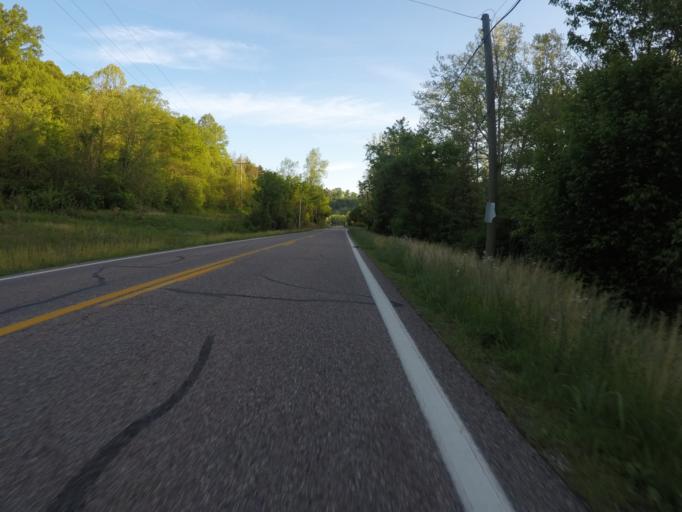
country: US
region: West Virginia
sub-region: Cabell County
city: Huntington
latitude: 38.4981
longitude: -82.4756
